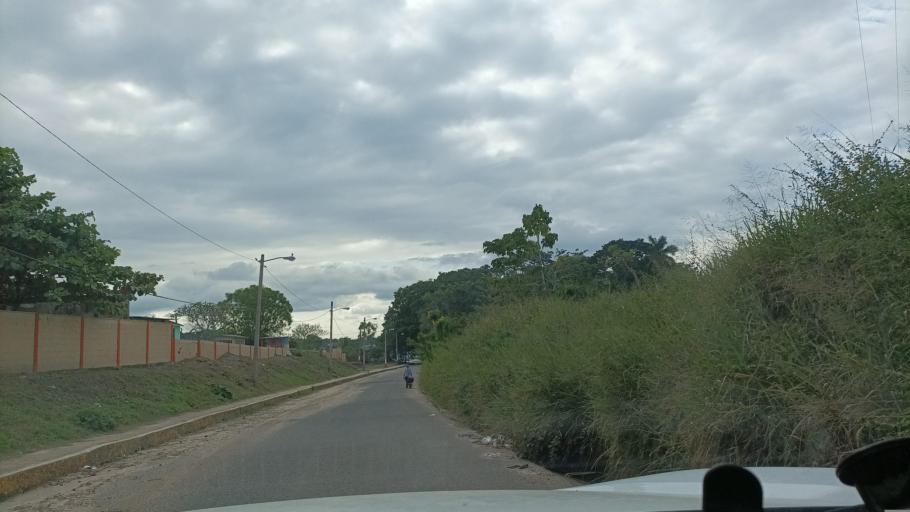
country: MX
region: Veracruz
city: Oluta
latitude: 17.9259
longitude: -94.8876
